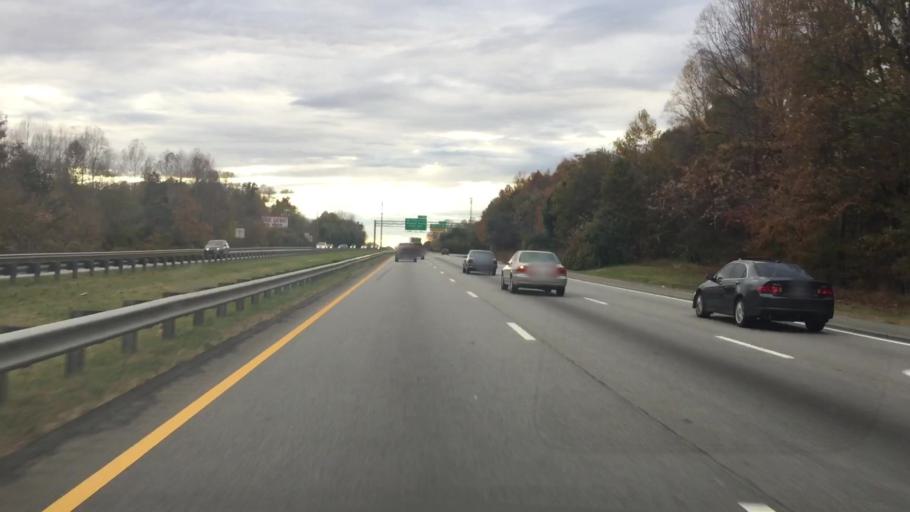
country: US
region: North Carolina
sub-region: Forsyth County
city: Winston-Salem
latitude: 36.0981
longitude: -80.2071
